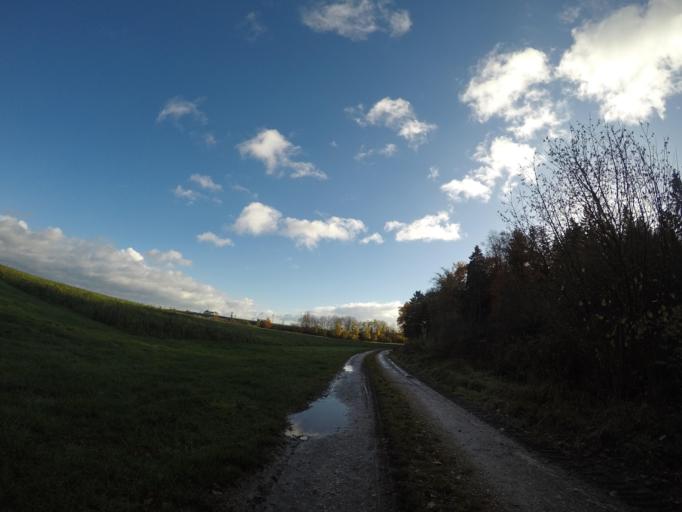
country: DE
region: Baden-Wuerttemberg
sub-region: Tuebingen Region
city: Bernstadt
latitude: 48.4554
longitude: 10.0223
